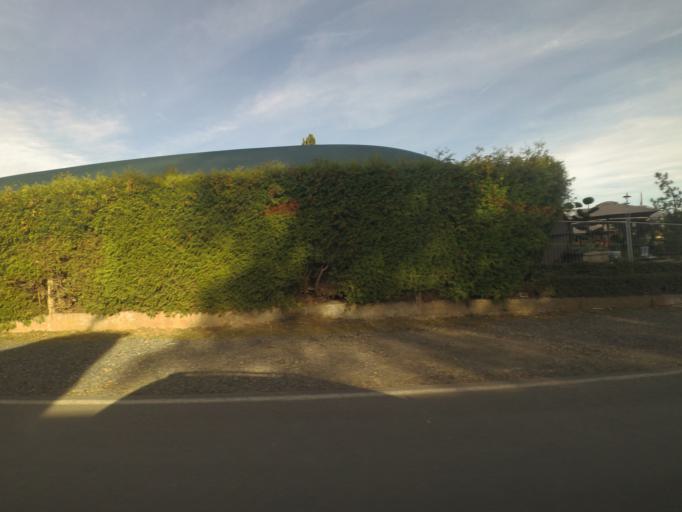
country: DE
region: Hesse
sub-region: Regierungsbezirk Kassel
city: Flieden
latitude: 50.4278
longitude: 9.5685
